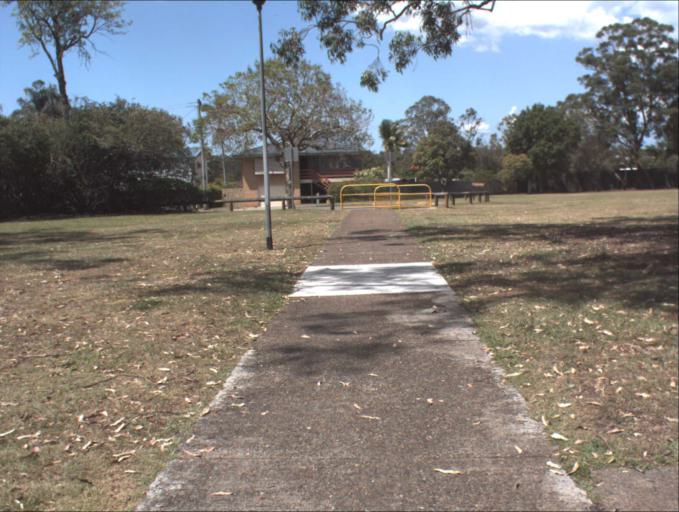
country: AU
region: Queensland
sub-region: Logan
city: Rochedale South
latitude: -27.5967
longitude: 153.1116
